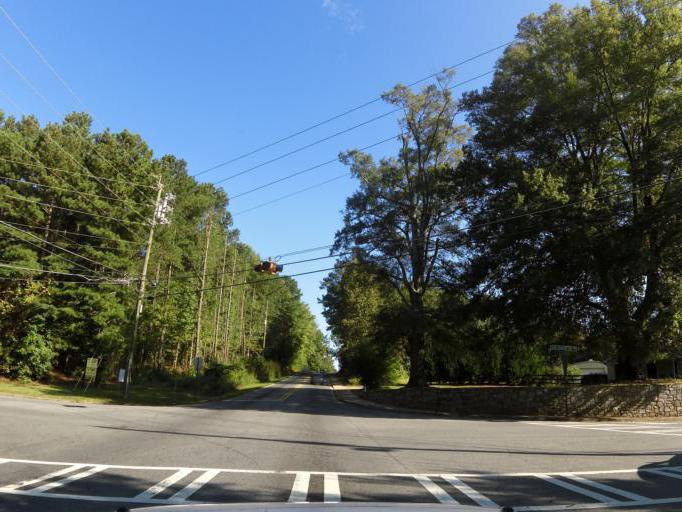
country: US
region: Georgia
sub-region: Cobb County
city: Acworth
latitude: 34.0156
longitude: -84.6755
